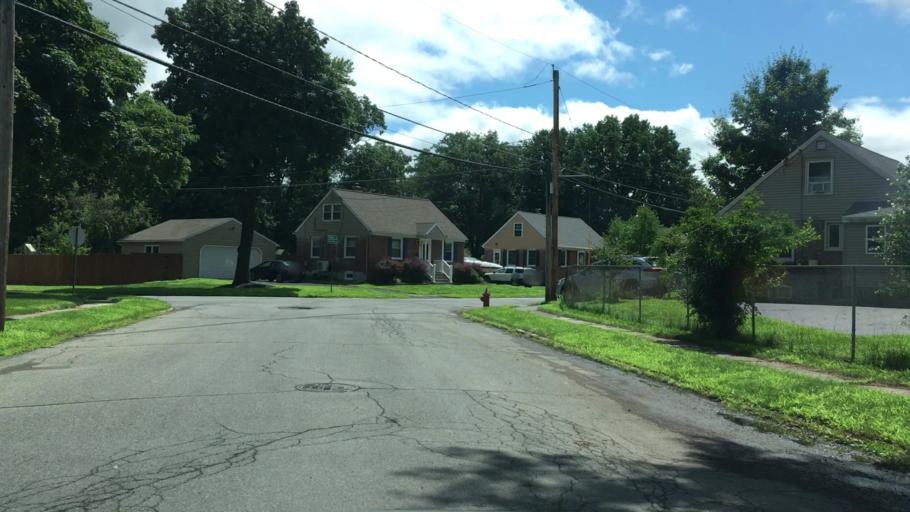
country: US
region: New York
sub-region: Albany County
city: Colonie
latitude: 42.7435
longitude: -73.8578
